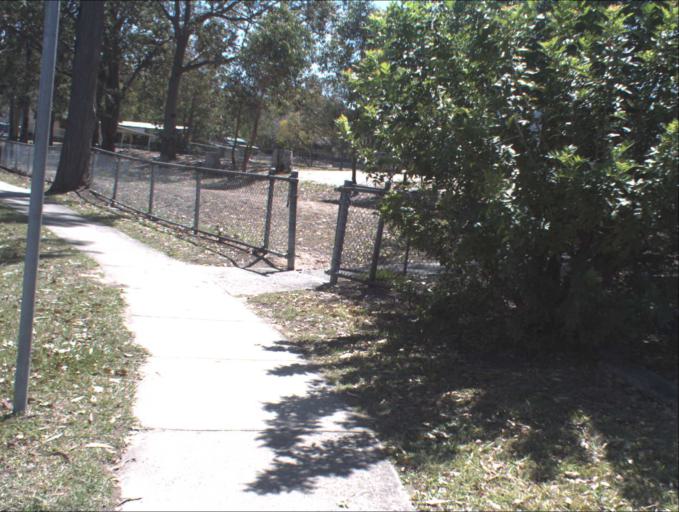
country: AU
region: Queensland
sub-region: Logan
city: Springwood
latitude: -27.6079
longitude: 153.1278
